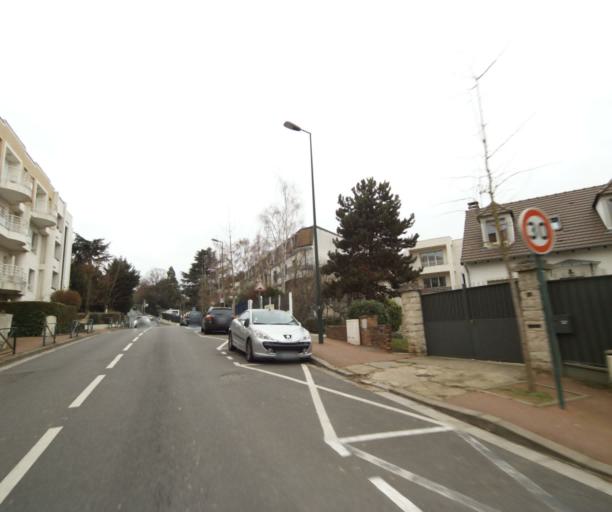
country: FR
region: Ile-de-France
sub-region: Departement des Hauts-de-Seine
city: Saint-Cloud
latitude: 48.8532
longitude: 2.1960
